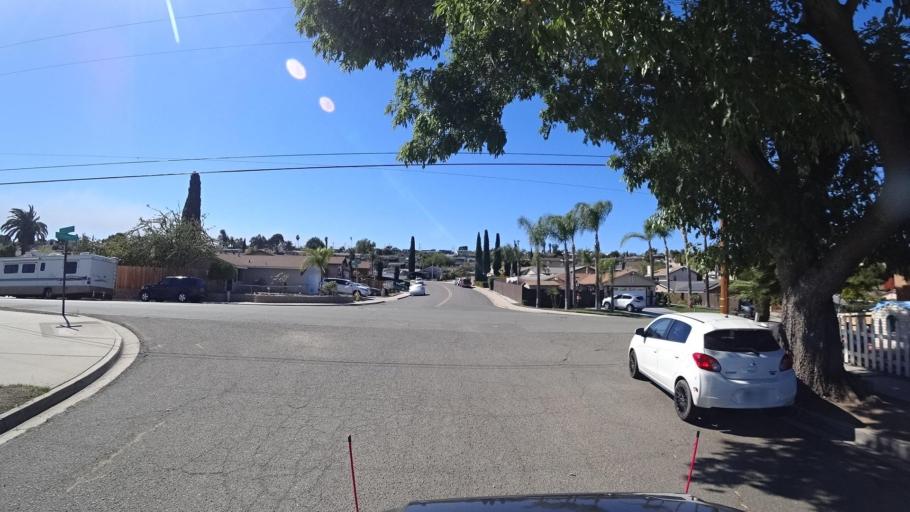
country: US
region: California
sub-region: San Diego County
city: La Presa
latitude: 32.7113
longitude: -117.0190
